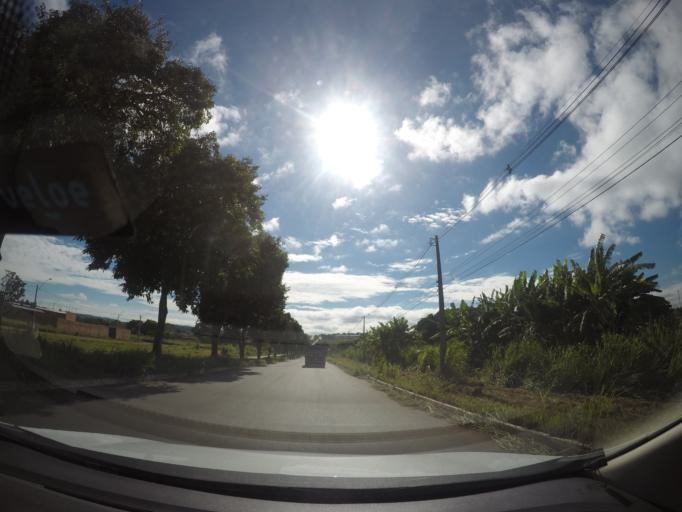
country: BR
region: Goias
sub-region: Goiania
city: Goiania
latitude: -16.6520
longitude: -49.1716
